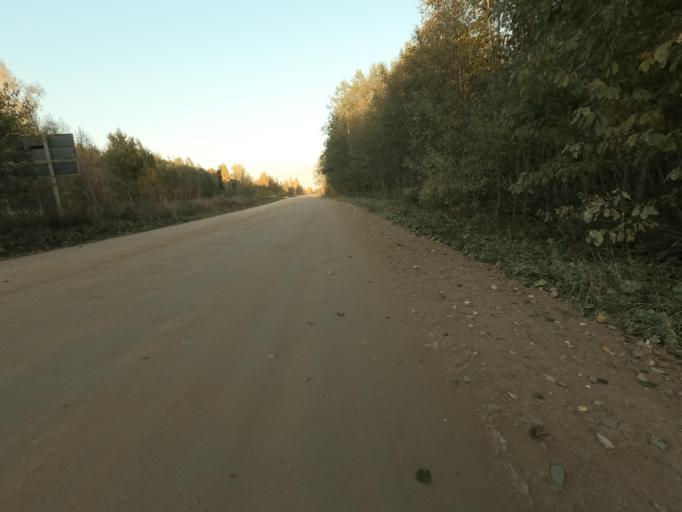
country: RU
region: Leningrad
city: Lyuban'
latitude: 59.0164
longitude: 31.0849
